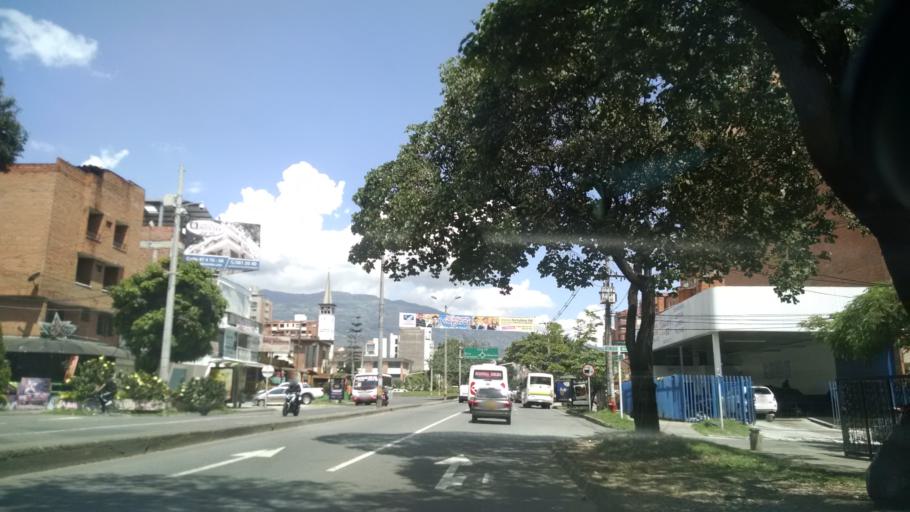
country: CO
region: Antioquia
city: Medellin
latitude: 6.2374
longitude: -75.6030
